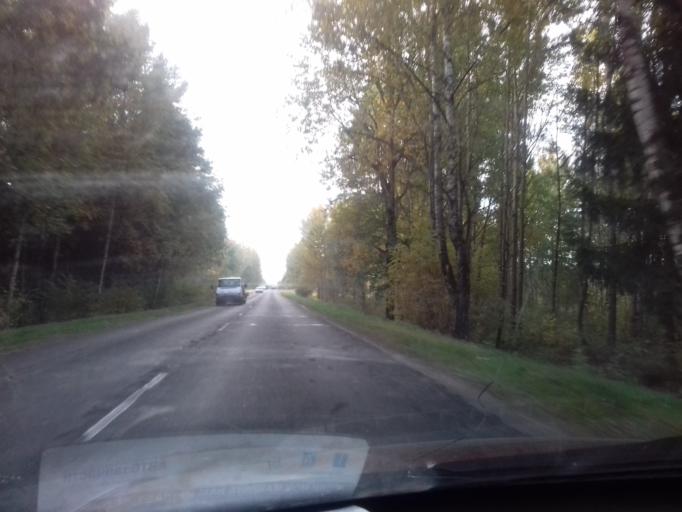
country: BY
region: Minsk
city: Hatava
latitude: 53.7607
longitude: 27.6496
